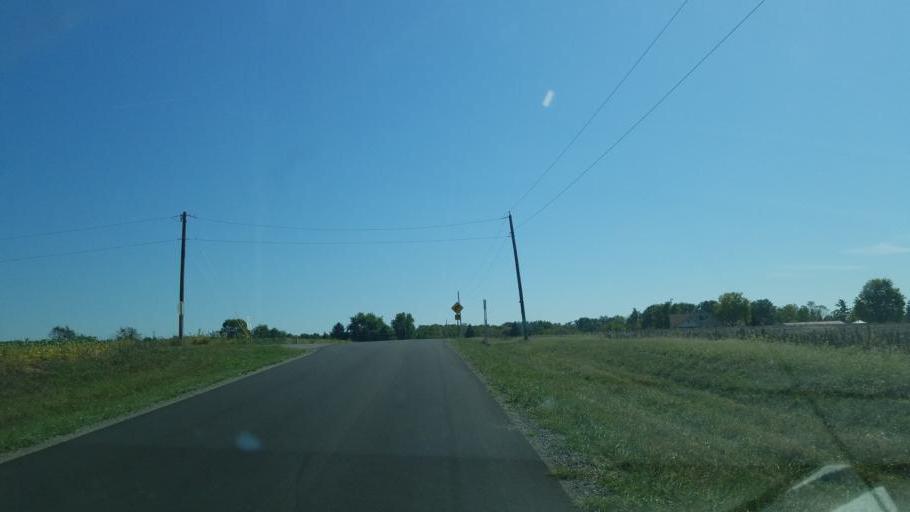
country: US
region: Ohio
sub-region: Logan County
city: Bellefontaine
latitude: 40.4054
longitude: -83.7700
